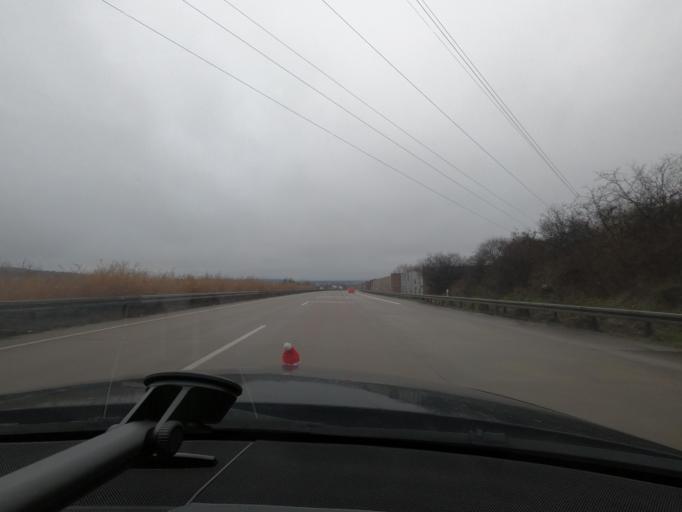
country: DE
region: Lower Saxony
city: Hildesheim
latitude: 52.1415
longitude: 10.0020
